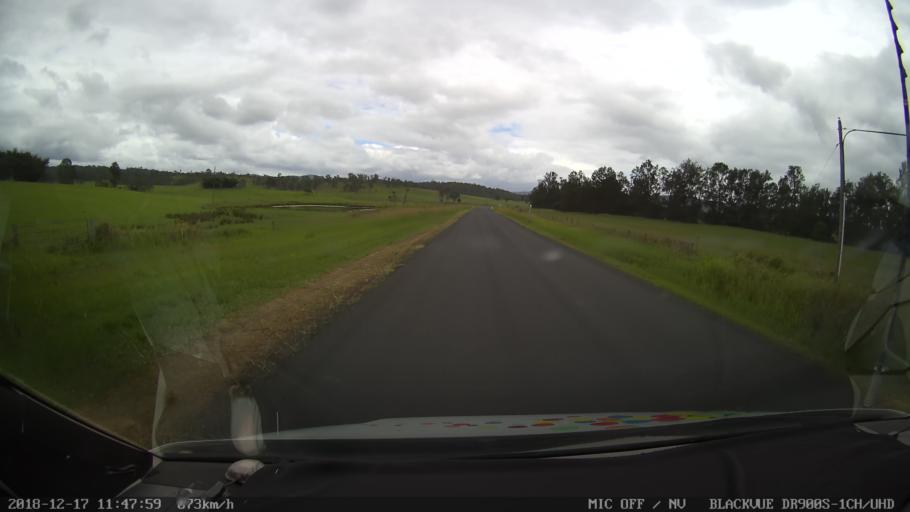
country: AU
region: New South Wales
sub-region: Kyogle
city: Kyogle
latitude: -28.6219
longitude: 152.5906
